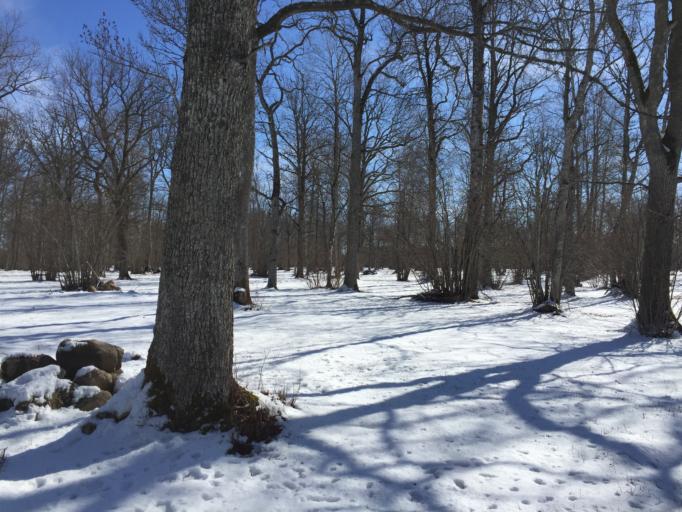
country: EE
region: Laeaene
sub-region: Lihula vald
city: Lihula
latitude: 58.5356
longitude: 24.0743
